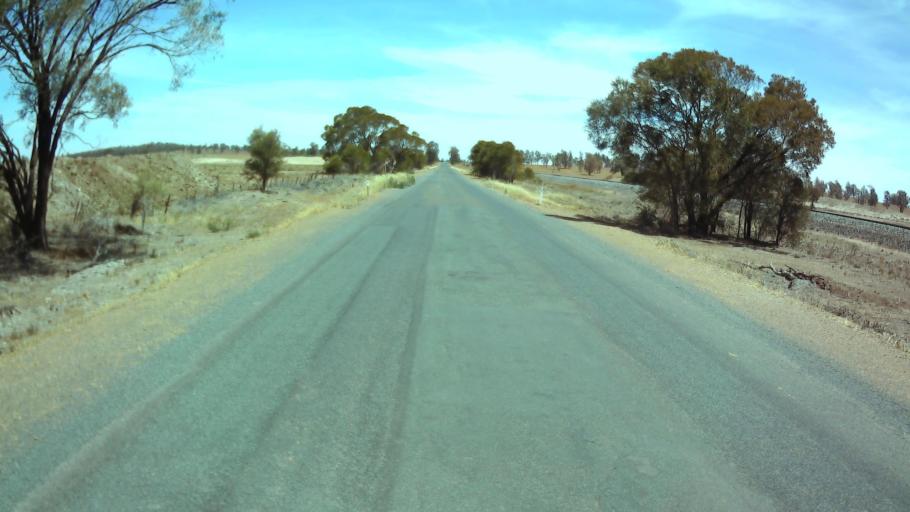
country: AU
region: New South Wales
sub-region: Weddin
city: Grenfell
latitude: -33.7647
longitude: 147.7594
